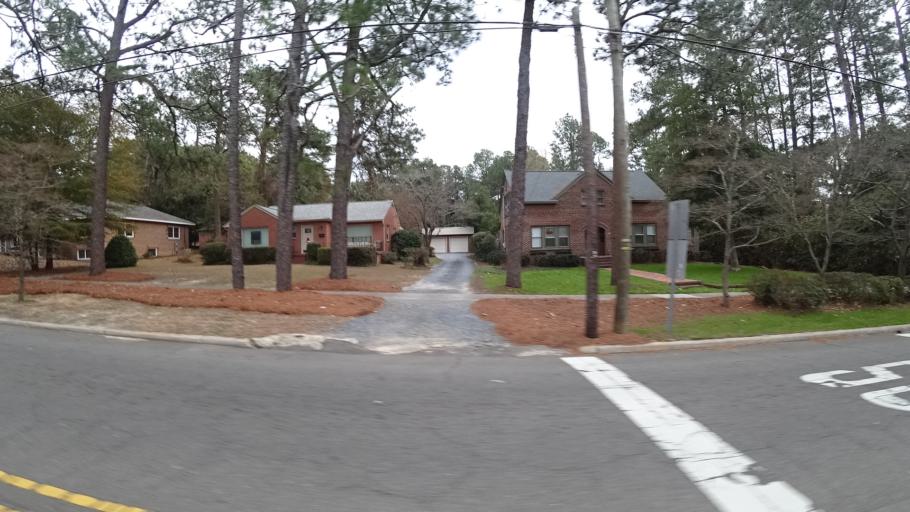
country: US
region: North Carolina
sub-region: Moore County
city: Southern Pines
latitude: 35.1714
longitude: -79.3904
